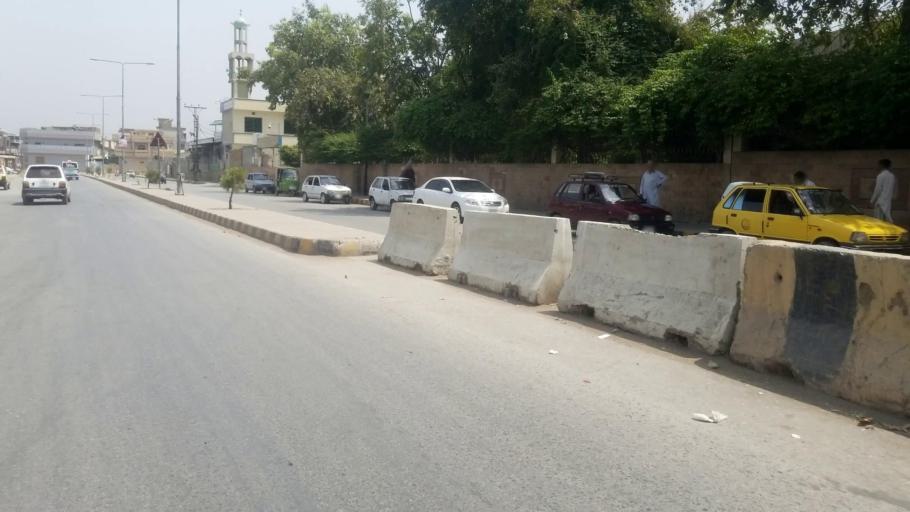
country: PK
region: Khyber Pakhtunkhwa
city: Peshawar
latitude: 33.9939
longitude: 71.4506
